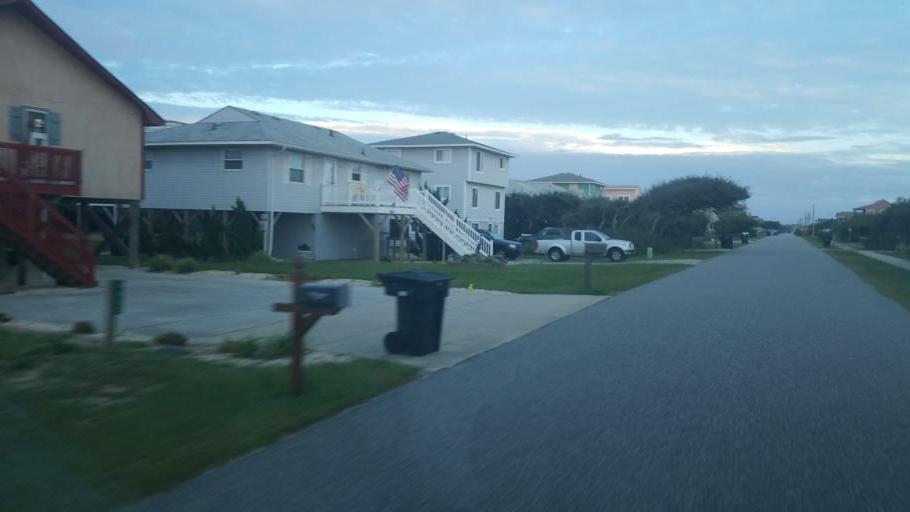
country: US
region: North Carolina
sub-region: Dare County
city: Kitty Hawk
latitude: 36.0824
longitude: -75.7020
